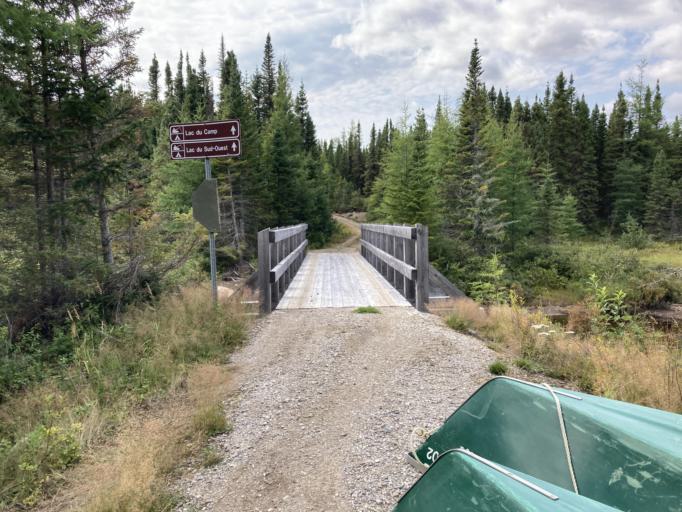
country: CA
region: Quebec
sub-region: Capitale-Nationale
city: Baie-Saint-Paul
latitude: 47.7188
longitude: -70.9196
